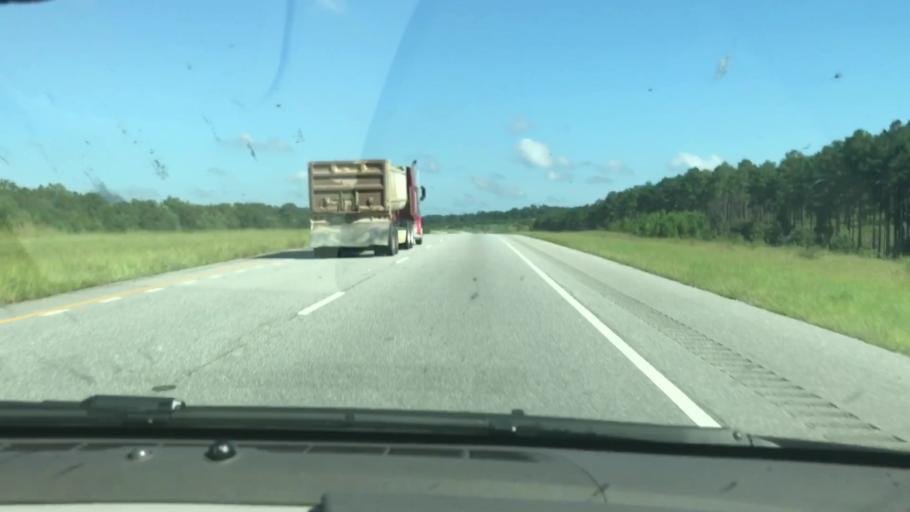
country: US
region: Alabama
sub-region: Barbour County
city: Eufaula
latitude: 32.1208
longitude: -85.1527
